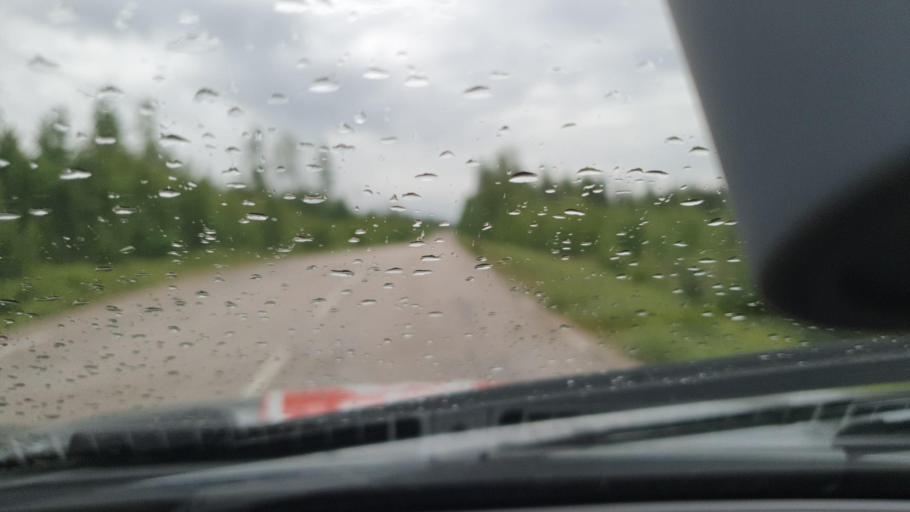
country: SE
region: Norrbotten
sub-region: Overkalix Kommun
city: OEverkalix
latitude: 66.4384
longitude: 22.7741
